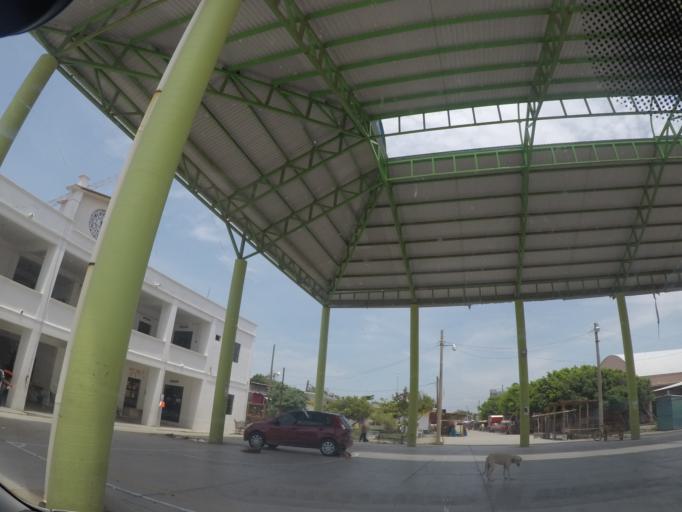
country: MX
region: Oaxaca
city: San Mateo del Mar
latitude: 16.2101
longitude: -94.9819
